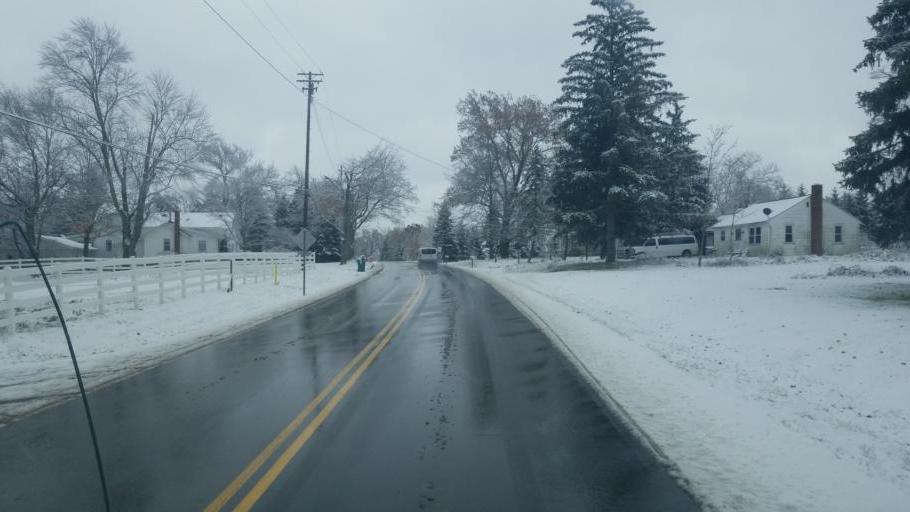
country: US
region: Ohio
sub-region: Geauga County
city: Middlefield
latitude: 41.4495
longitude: -81.0985
